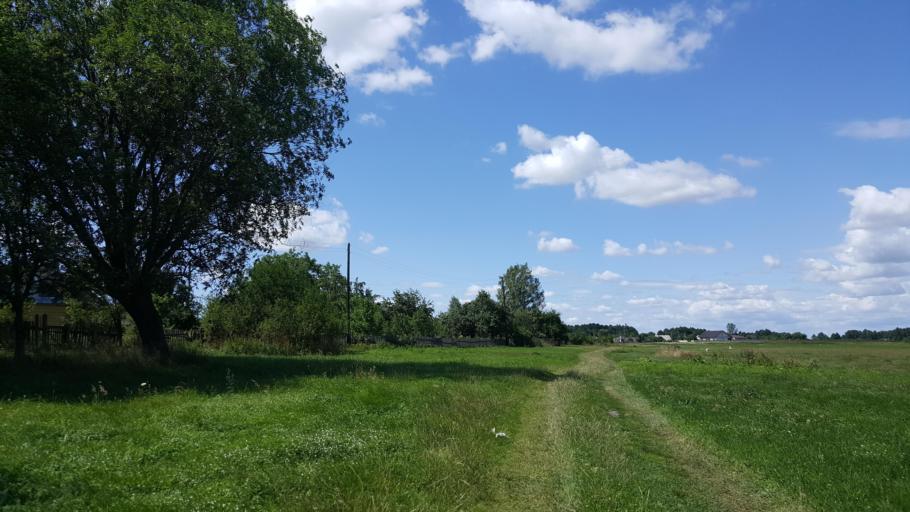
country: BY
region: Brest
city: Kamyanyets
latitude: 52.3872
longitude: 23.8081
